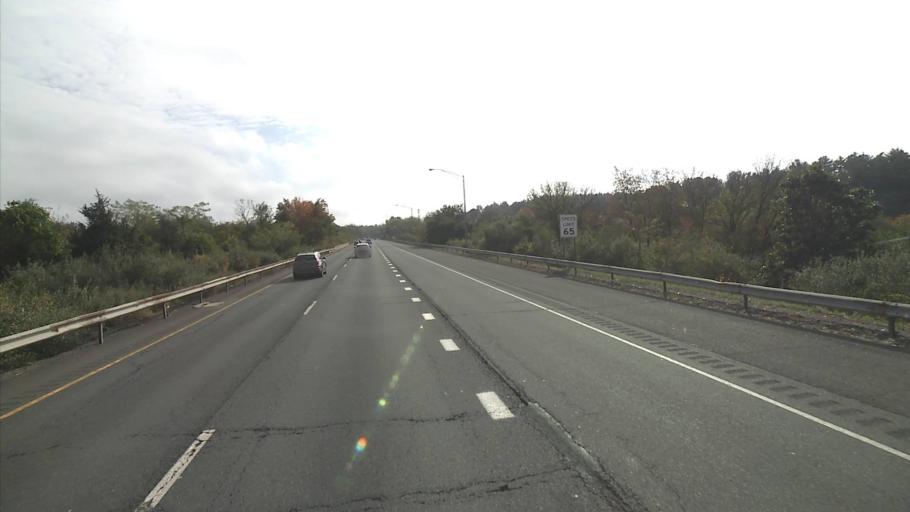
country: US
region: Connecticut
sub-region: Fairfield County
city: Newtown
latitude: 41.4153
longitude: -73.2798
